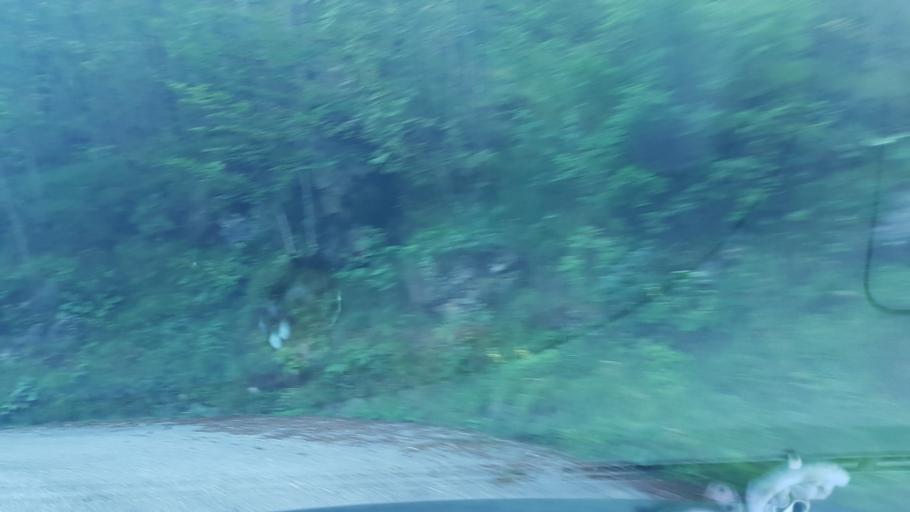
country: IT
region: Friuli Venezia Giulia
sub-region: Provincia di Pordenone
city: Frisanco
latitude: 46.2592
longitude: 12.7036
